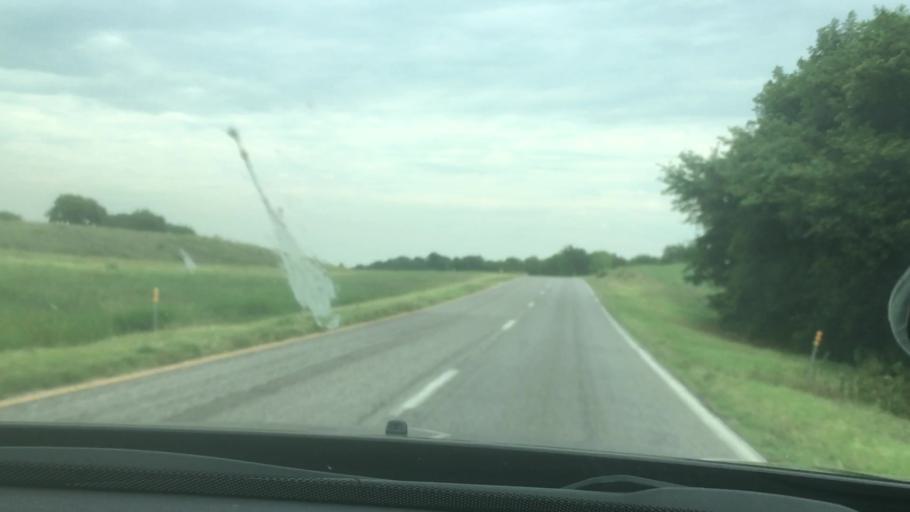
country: US
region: Oklahoma
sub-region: Pontotoc County
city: Ada
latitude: 34.6895
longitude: -96.7472
